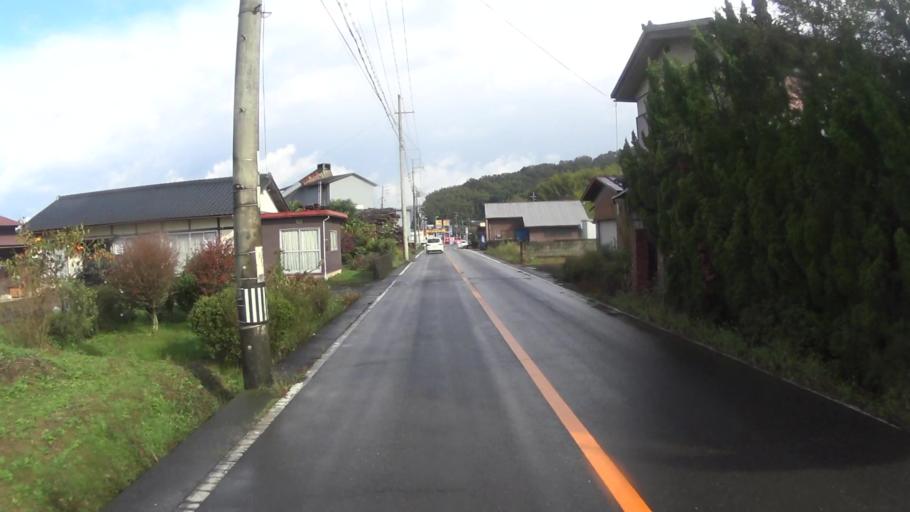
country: JP
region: Kyoto
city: Ayabe
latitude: 35.3376
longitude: 135.2157
